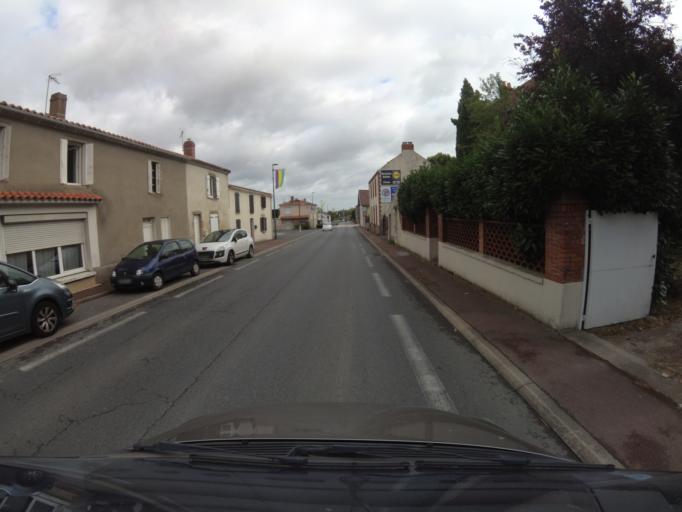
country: FR
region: Pays de la Loire
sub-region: Departement de la Vendee
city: Cugand
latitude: 47.0618
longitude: -1.2564
